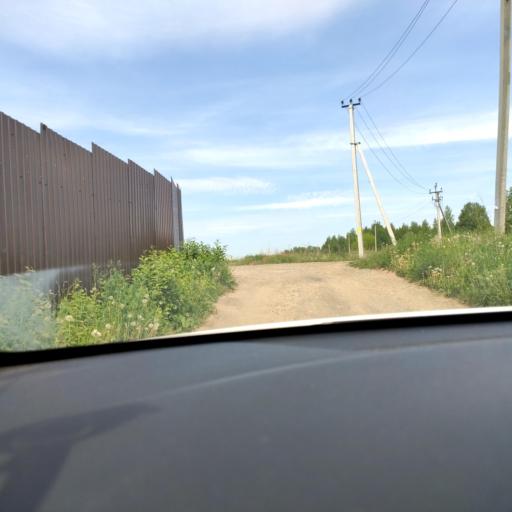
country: RU
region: Tatarstan
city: Vysokaya Gora
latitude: 55.9948
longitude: 49.3257
